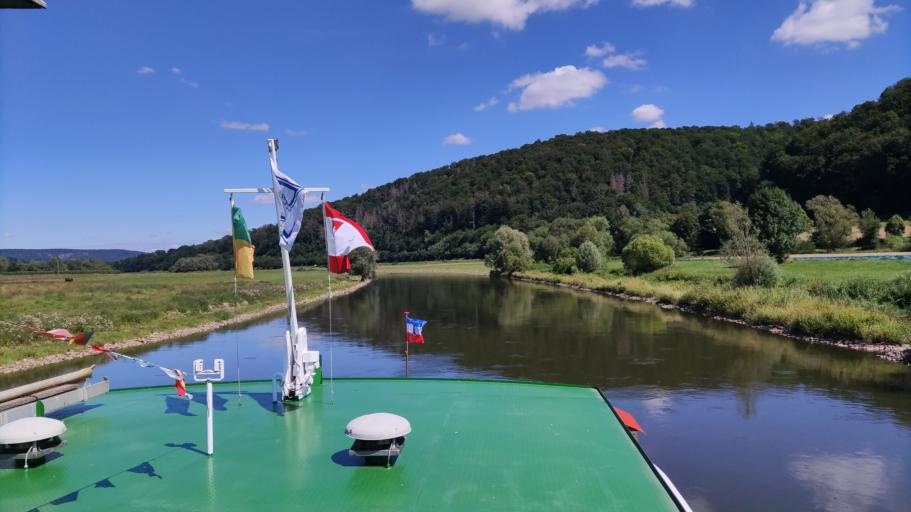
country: DE
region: Lower Saxony
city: Derental
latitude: 51.7004
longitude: 9.4016
